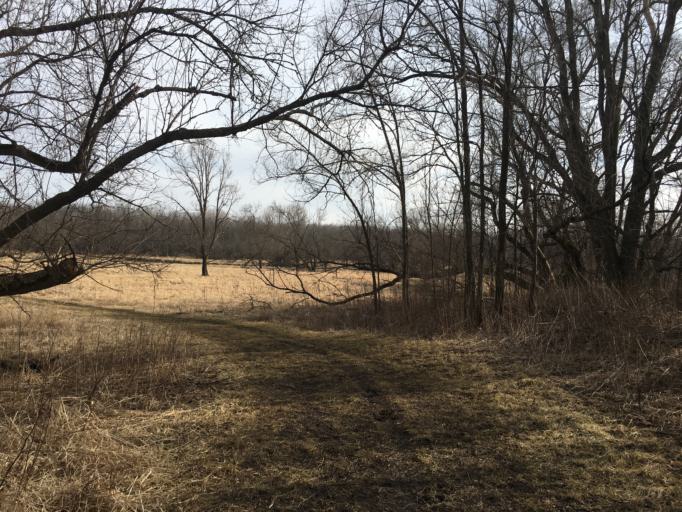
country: US
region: Illinois
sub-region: Cook County
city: Streamwood
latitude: 42.0497
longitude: -88.2057
